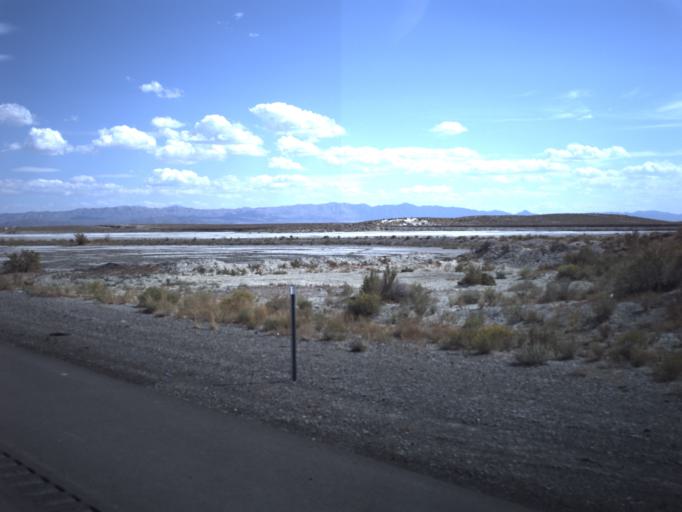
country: US
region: Utah
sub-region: Tooele County
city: Wendover
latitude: 40.7267
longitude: -113.2792
